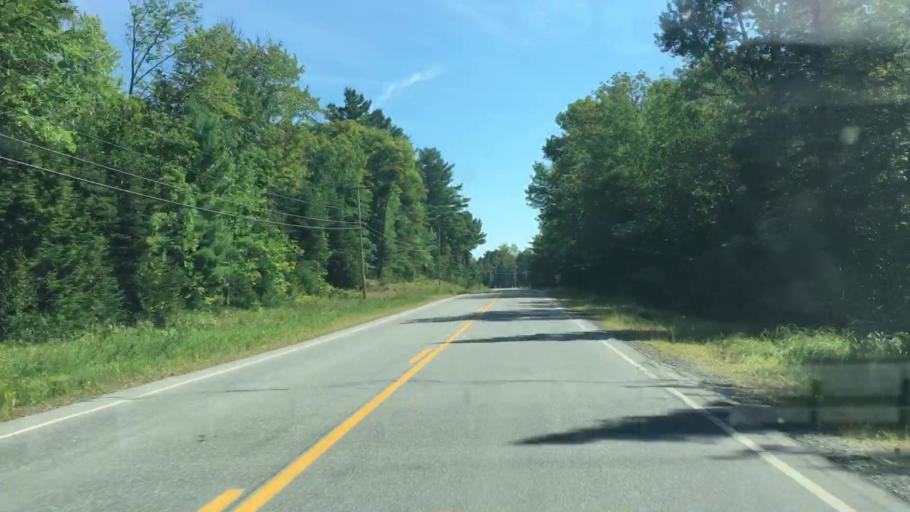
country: US
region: Maine
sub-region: Piscataquis County
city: Milo
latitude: 45.1914
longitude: -68.8983
